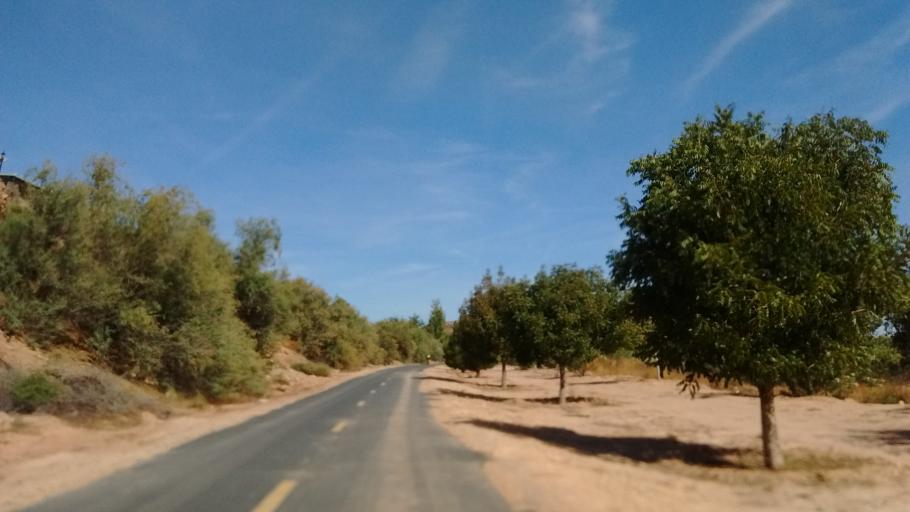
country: US
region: Utah
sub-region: Washington County
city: Saint George
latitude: 37.0584
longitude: -113.6003
